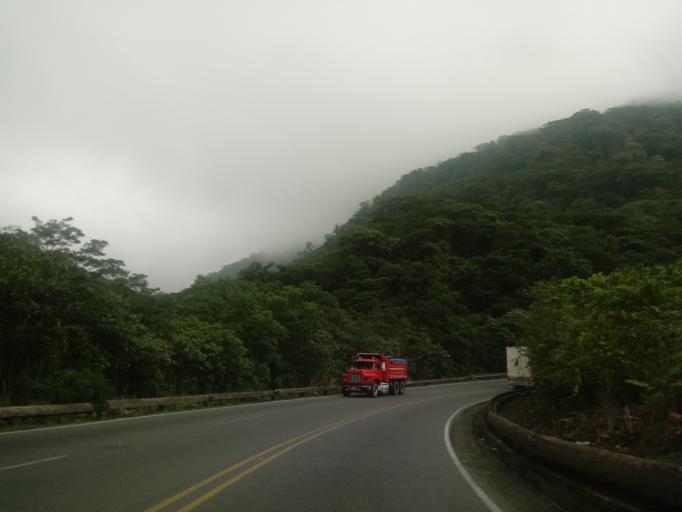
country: CR
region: Heredia
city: Angeles
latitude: 10.0561
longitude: -84.0136
